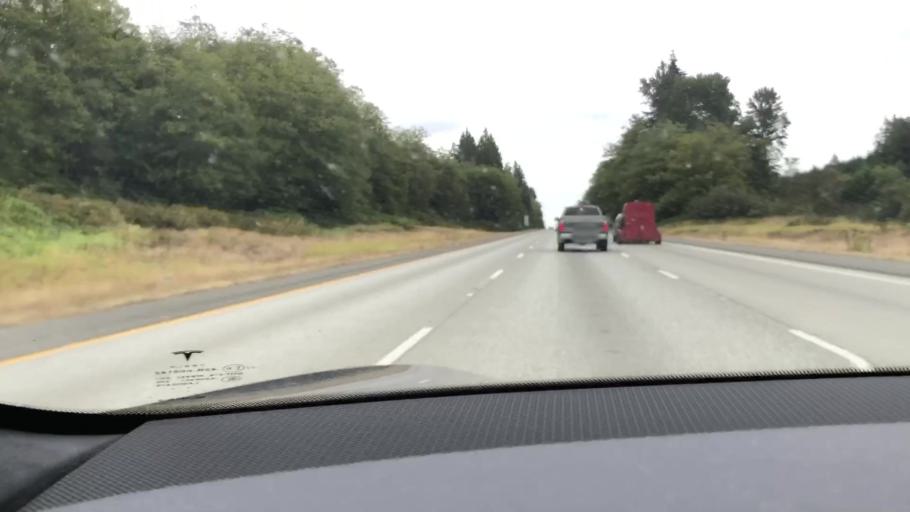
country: US
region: Washington
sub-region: Snohomish County
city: Bryant
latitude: 48.2607
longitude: -122.2629
